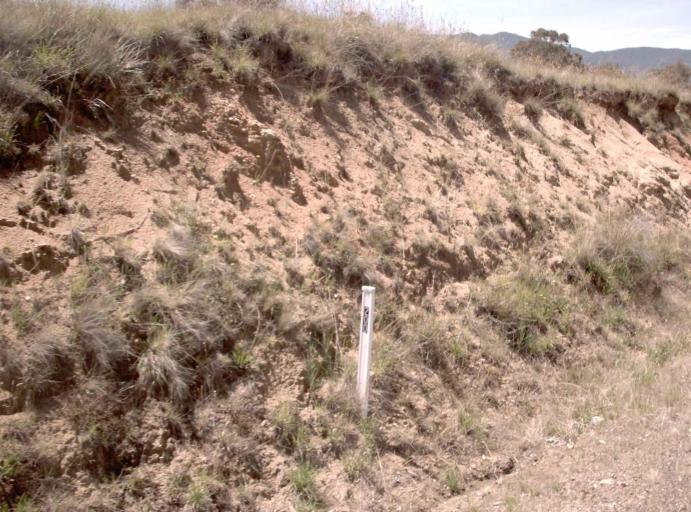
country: AU
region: Victoria
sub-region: East Gippsland
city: Bairnsdale
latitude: -37.1702
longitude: 147.6904
